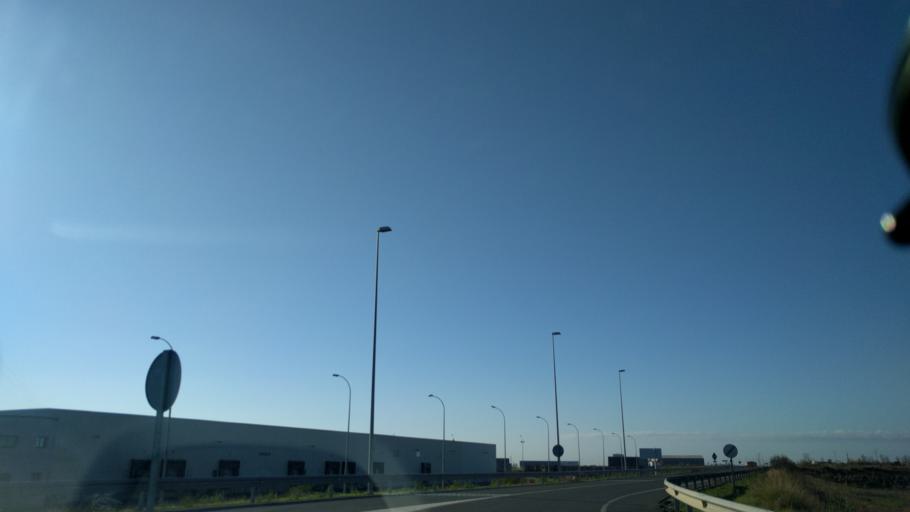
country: ES
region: Catalonia
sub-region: Provincia de Lleida
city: Termens
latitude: 41.7076
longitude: 0.7516
